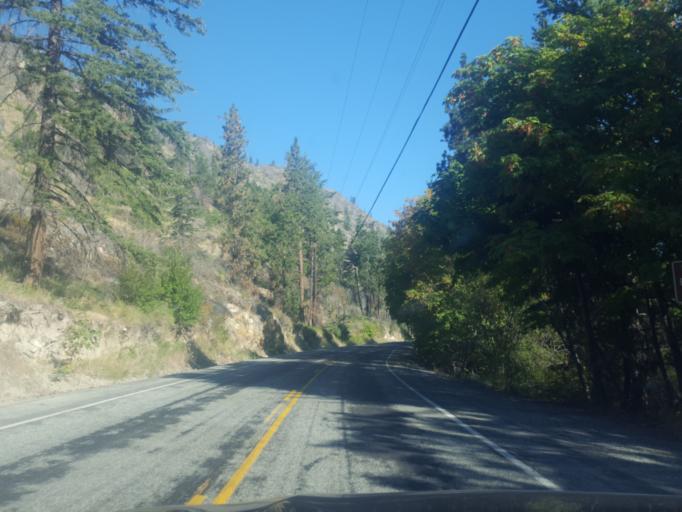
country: US
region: Washington
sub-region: Chelan County
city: Granite Falls
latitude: 47.9686
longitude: -120.2147
